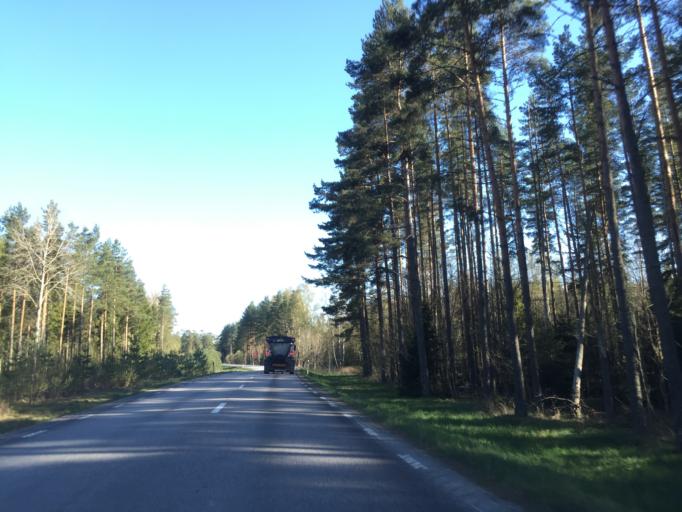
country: SE
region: OErebro
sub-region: Hallsbergs Kommun
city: Skollersta
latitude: 59.2408
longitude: 15.4028
